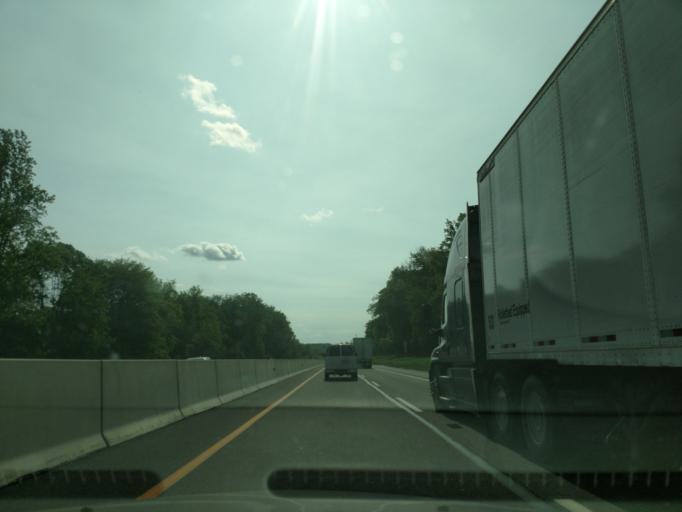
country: US
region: Pennsylvania
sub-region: Lancaster County
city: Clay
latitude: 40.2370
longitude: -76.2752
